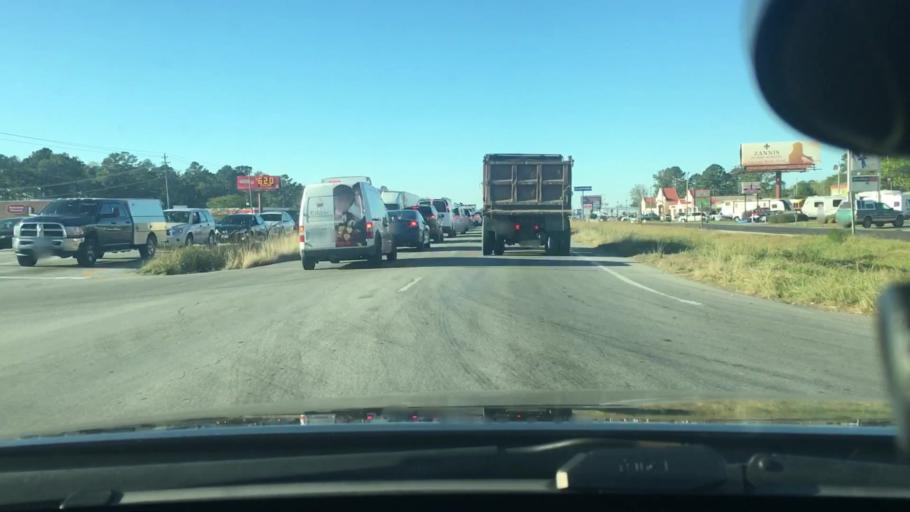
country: US
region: North Carolina
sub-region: Craven County
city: James City
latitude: 35.0748
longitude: -77.0278
